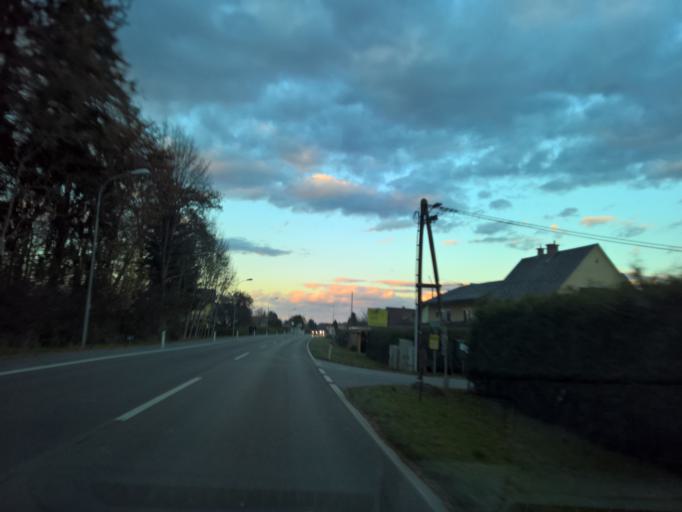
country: AT
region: Styria
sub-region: Politischer Bezirk Graz-Umgebung
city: Werndorf
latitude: 46.9378
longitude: 15.4832
